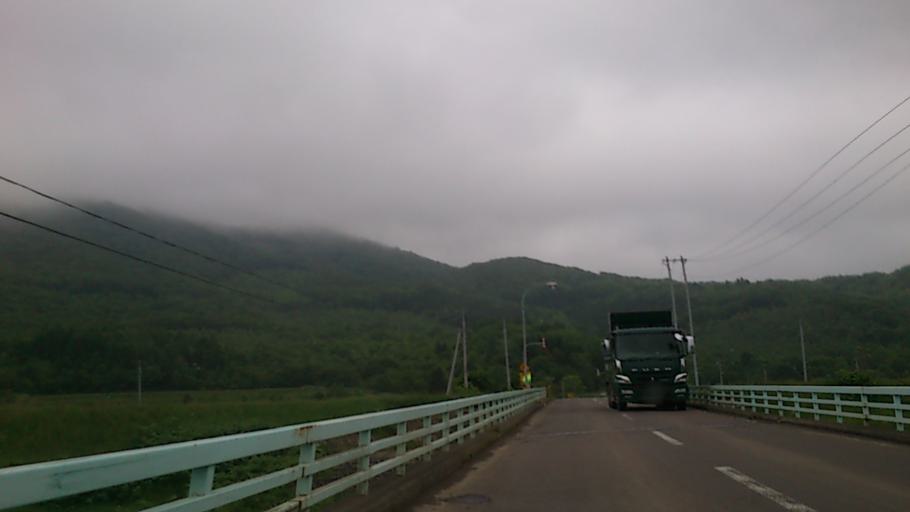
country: JP
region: Hokkaido
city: Iwanai
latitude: 42.7949
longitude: 140.4801
